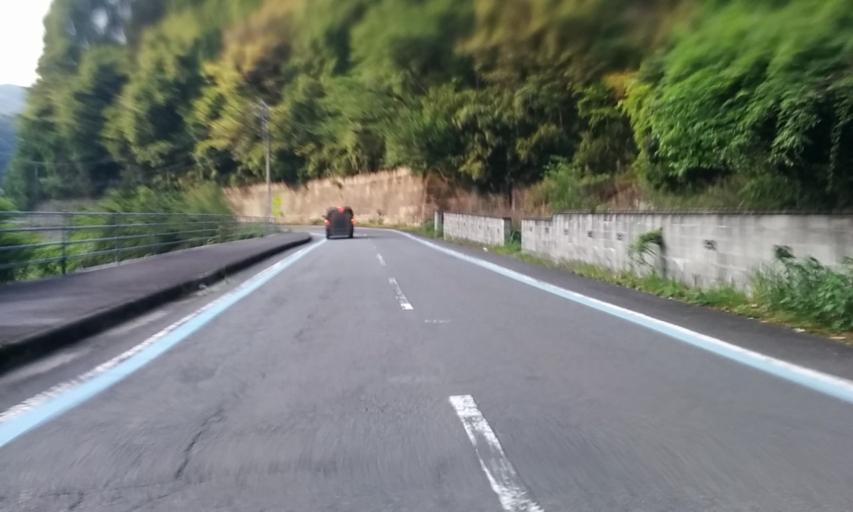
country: JP
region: Ehime
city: Saijo
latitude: 33.8720
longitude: 133.1762
